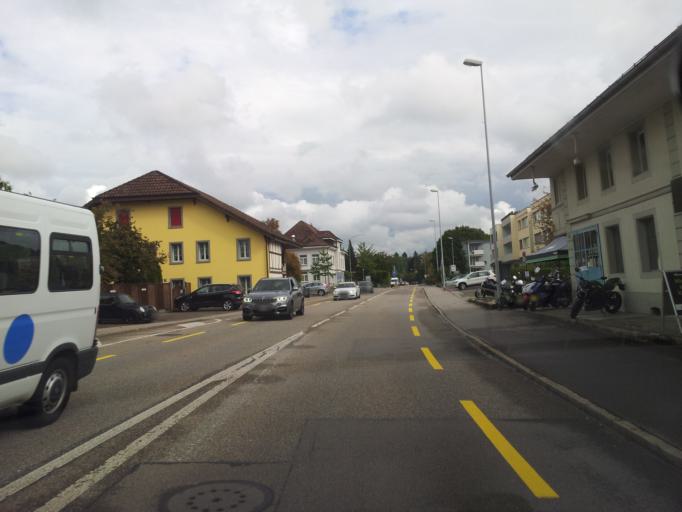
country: CH
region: Aargau
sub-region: Bezirk Zofingen
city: Rothrist
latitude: 47.3056
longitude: 7.8903
